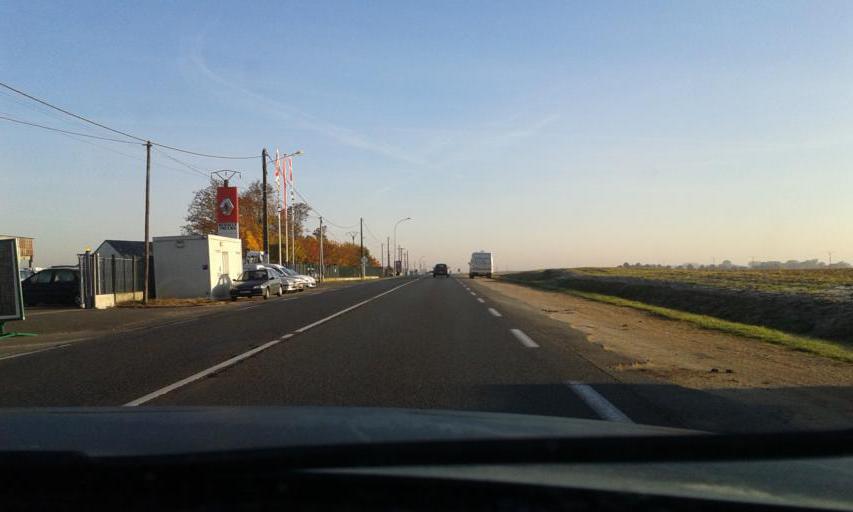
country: FR
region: Centre
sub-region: Departement du Loiret
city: Beaugency
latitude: 47.7868
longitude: 1.6397
